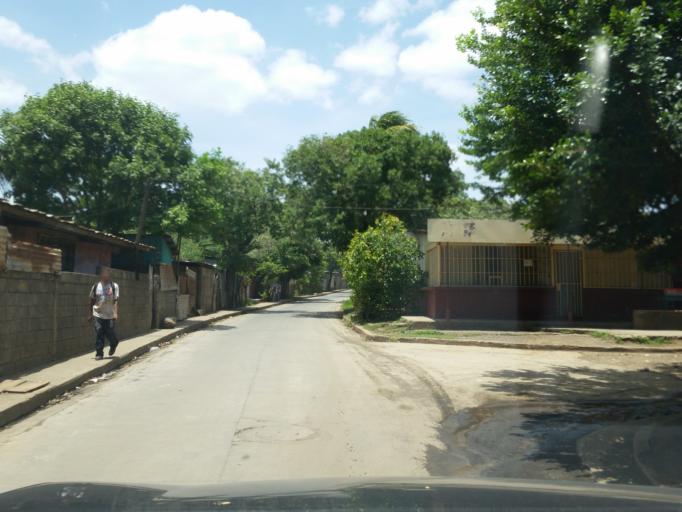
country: NI
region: Managua
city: Managua
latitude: 12.1191
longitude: -86.2422
